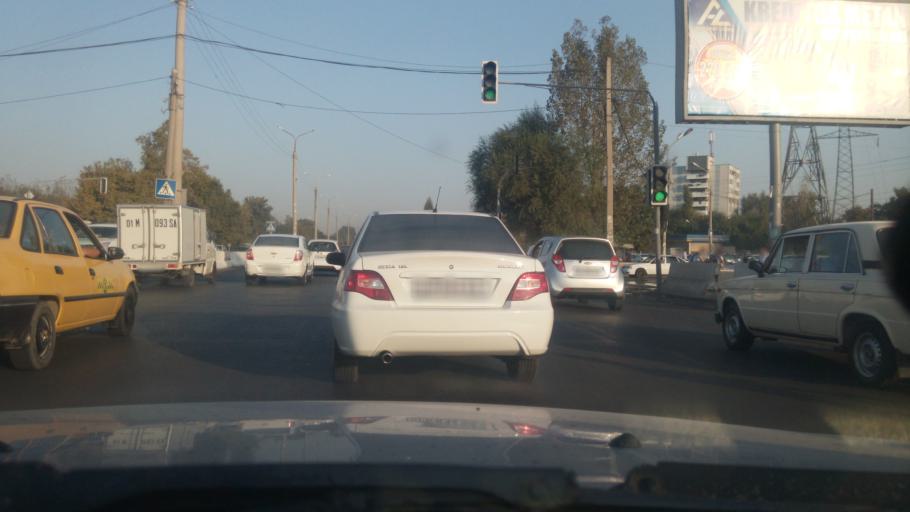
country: UZ
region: Toshkent Shahri
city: Tashkent
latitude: 41.2550
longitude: 69.1572
